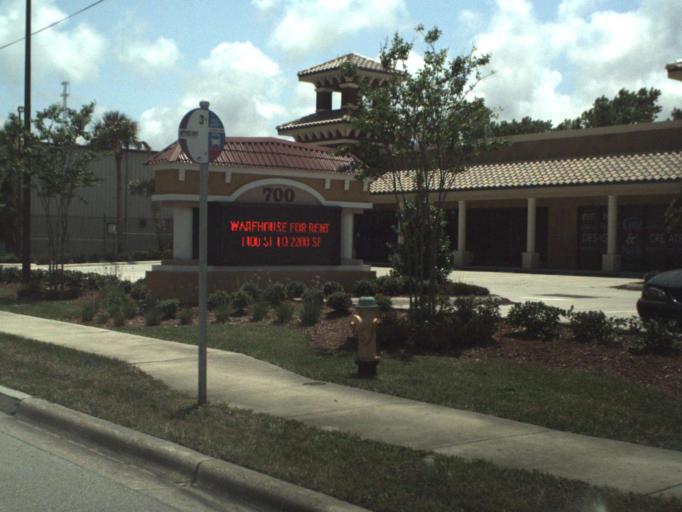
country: US
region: Florida
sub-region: Volusia County
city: Holly Hill
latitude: 29.2377
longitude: -81.0373
